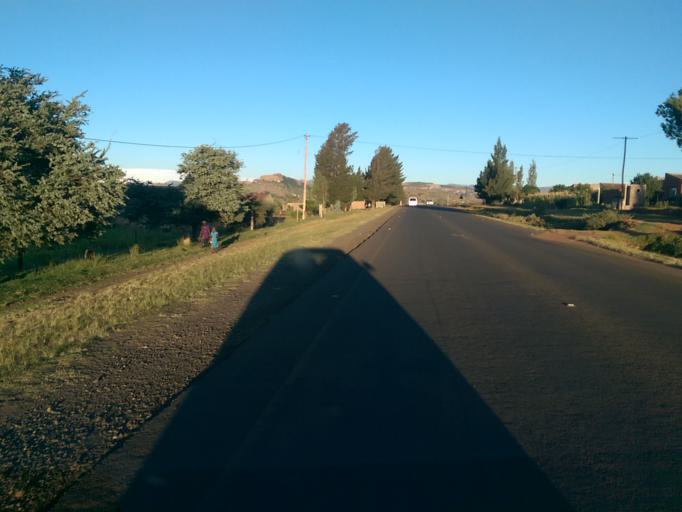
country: LS
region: Maseru
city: Maseru
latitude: -29.4087
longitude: 27.5875
